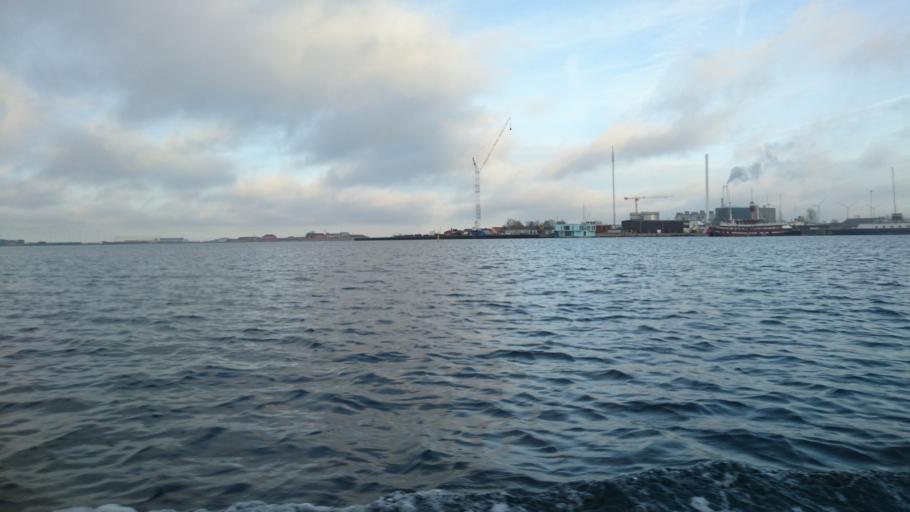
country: DK
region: Capital Region
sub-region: Kobenhavn
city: Christianshavn
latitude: 55.6932
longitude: 12.6031
